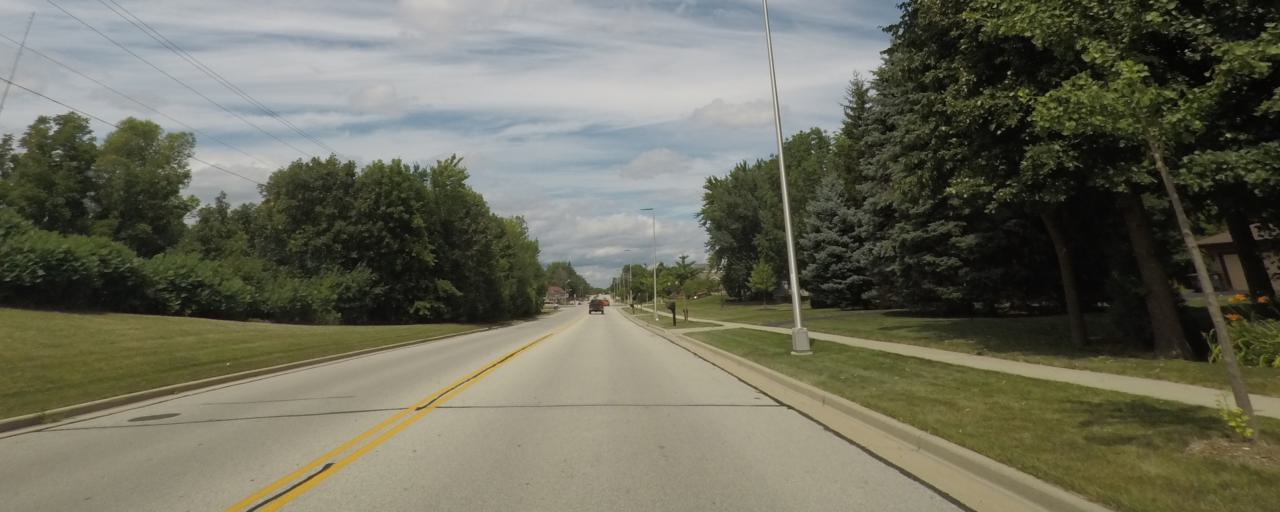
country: US
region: Wisconsin
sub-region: Milwaukee County
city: Hales Corners
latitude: 42.9610
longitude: -88.0693
